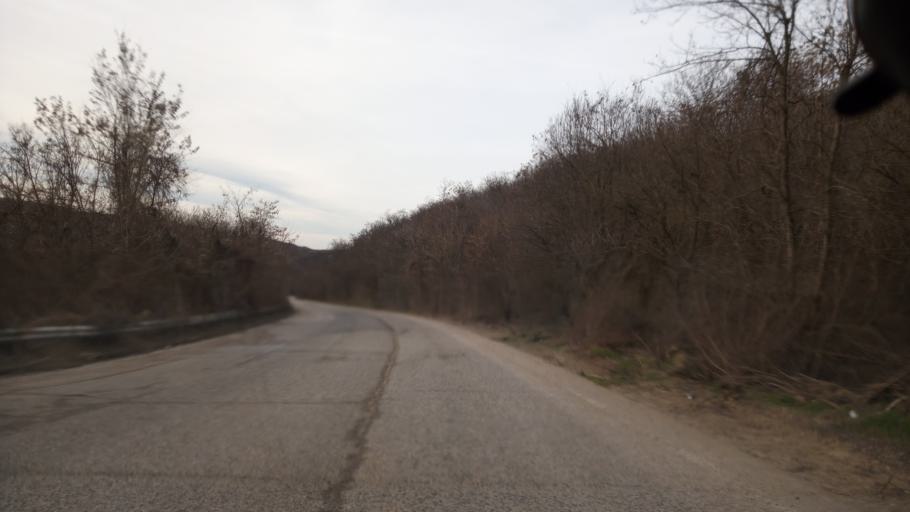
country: BG
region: Pleven
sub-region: Obshtina Nikopol
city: Nikopol
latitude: 43.5933
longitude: 24.9510
